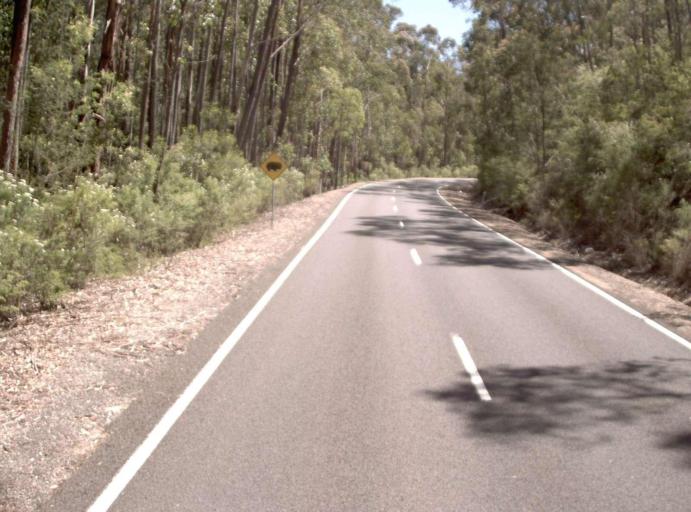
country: AU
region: Victoria
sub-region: East Gippsland
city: Lakes Entrance
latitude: -37.3627
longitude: 148.2207
